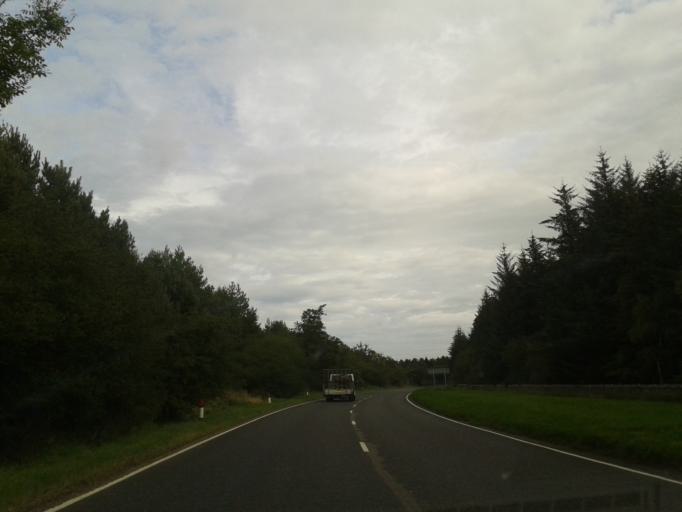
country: GB
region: Scotland
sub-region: Moray
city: Findochty
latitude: 57.6843
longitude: -2.8856
